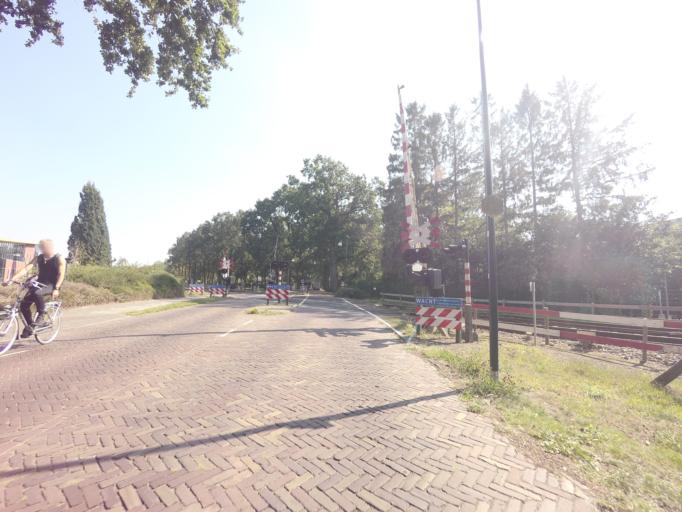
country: NL
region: Groningen
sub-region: Gemeente Zuidhorn
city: Zuidhorn
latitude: 53.2494
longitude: 6.4037
